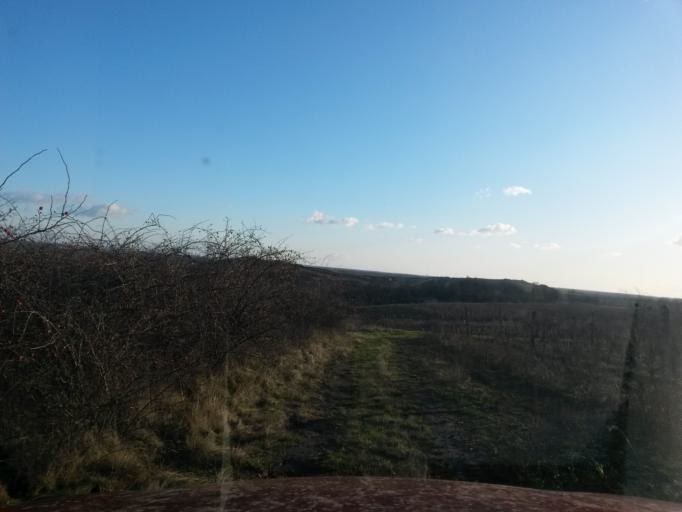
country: HU
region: Borsod-Abauj-Zemplen
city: Sarospatak
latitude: 48.3224
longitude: 21.5382
